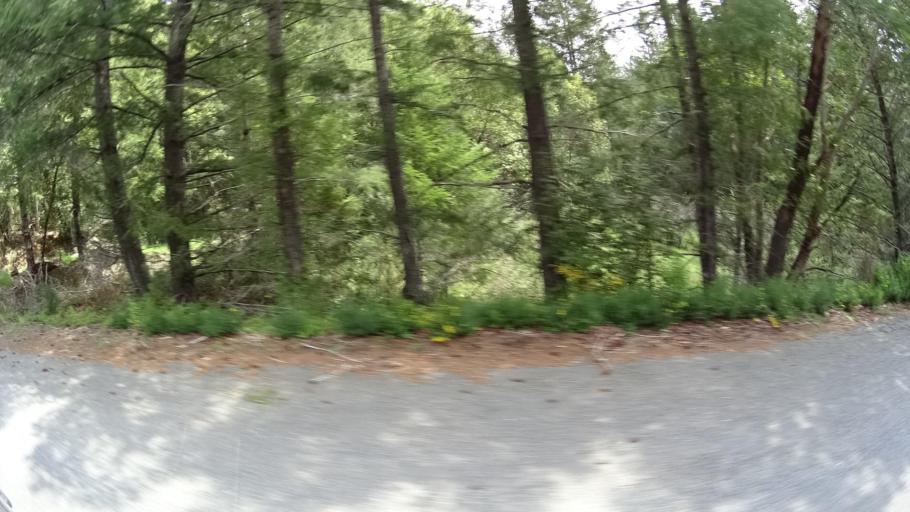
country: US
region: California
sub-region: Humboldt County
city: Redway
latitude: 40.0526
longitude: -123.9557
